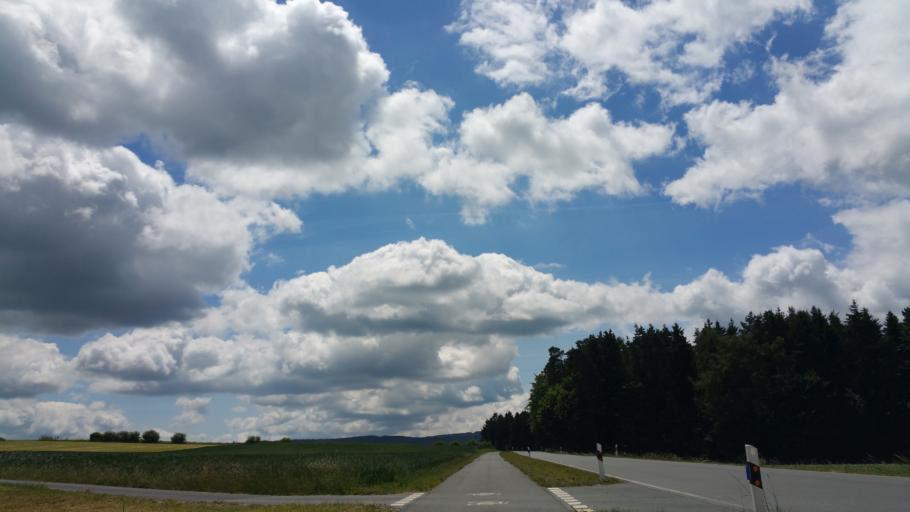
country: DE
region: Bavaria
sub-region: Upper Franconia
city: Schwarzenbach an der Saale
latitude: 50.2020
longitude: 11.9268
